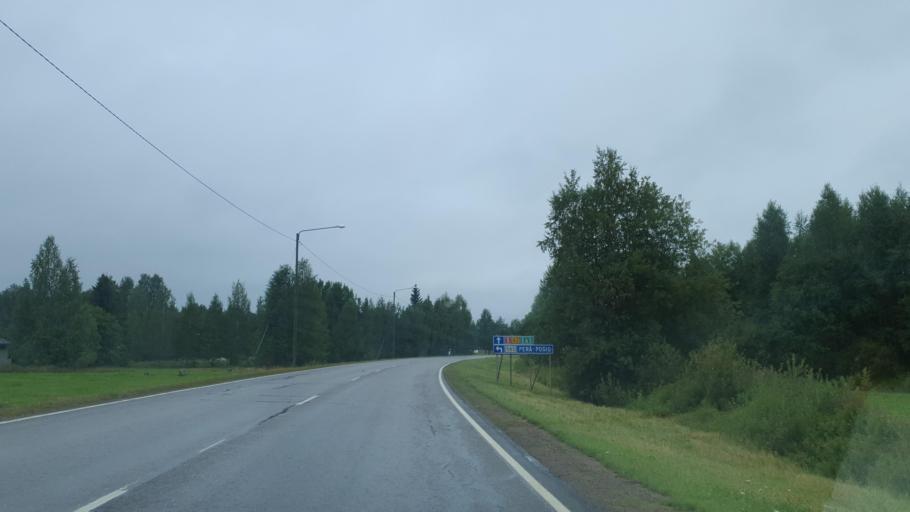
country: FI
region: Lapland
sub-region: Itae-Lappi
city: Kemijaervi
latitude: 66.6934
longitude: 27.5658
